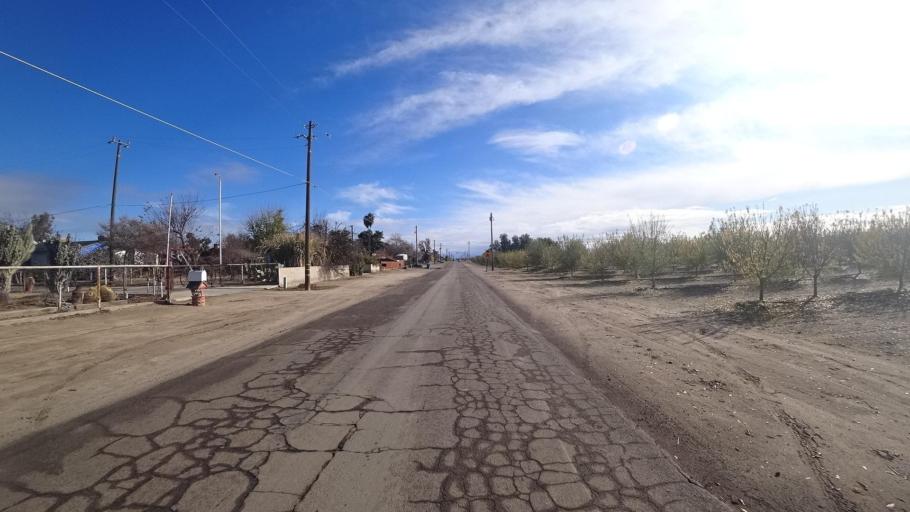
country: US
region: California
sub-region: Kern County
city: Rosedale
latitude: 35.3835
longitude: -119.2553
